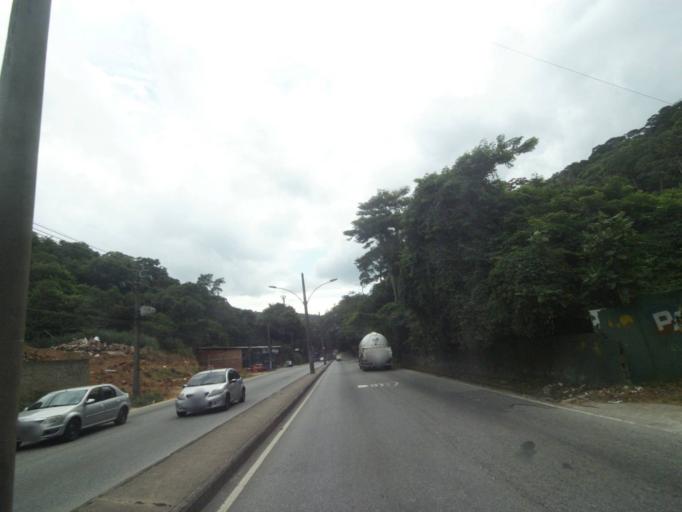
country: BR
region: Rio de Janeiro
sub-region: Nilopolis
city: Nilopolis
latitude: -22.8994
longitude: -43.3937
